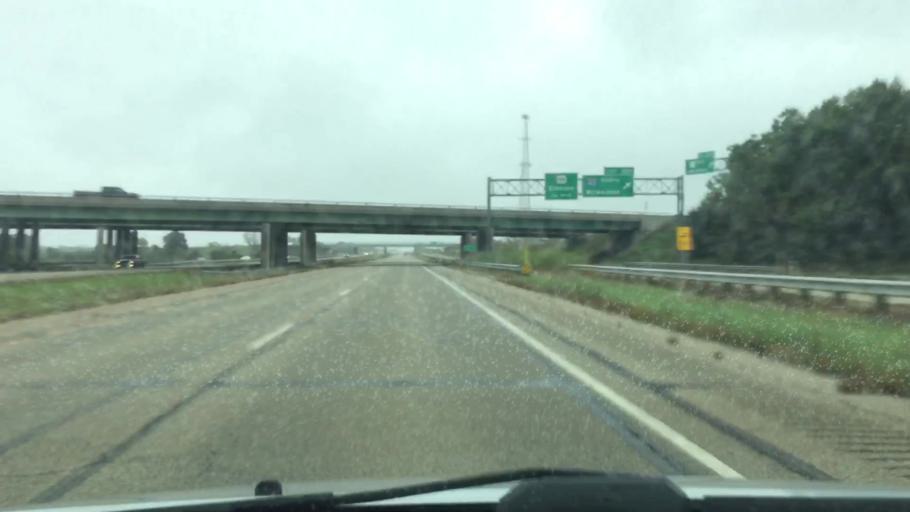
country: US
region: Wisconsin
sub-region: Walworth County
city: Elkhorn
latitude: 42.6756
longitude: -88.5228
